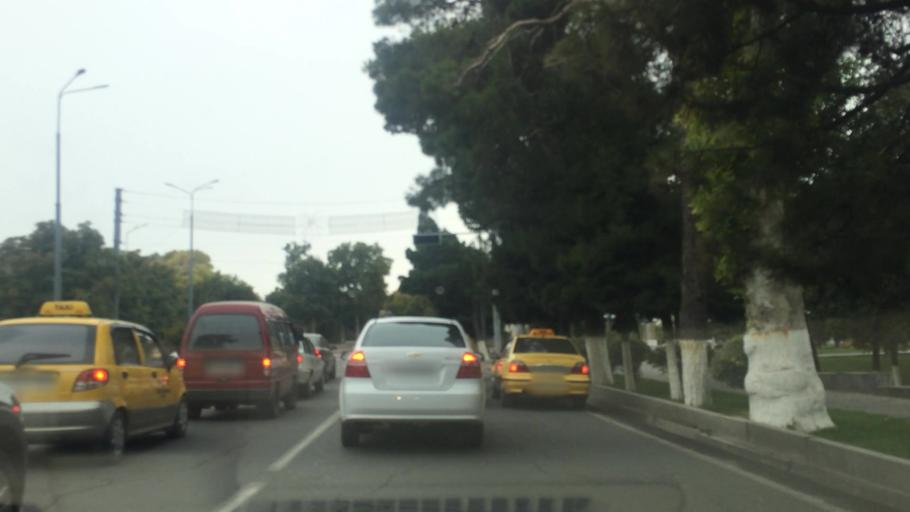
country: UZ
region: Samarqand
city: Samarqand
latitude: 39.6511
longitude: 66.9665
